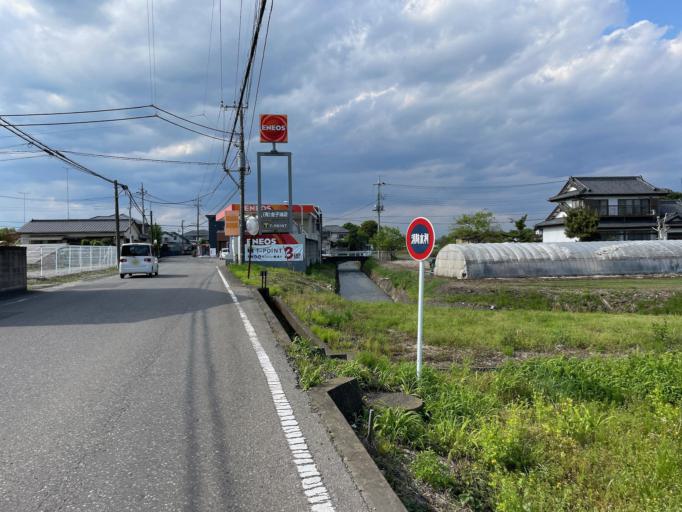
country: JP
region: Tochigi
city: Tochigi
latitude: 36.4160
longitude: 139.7323
